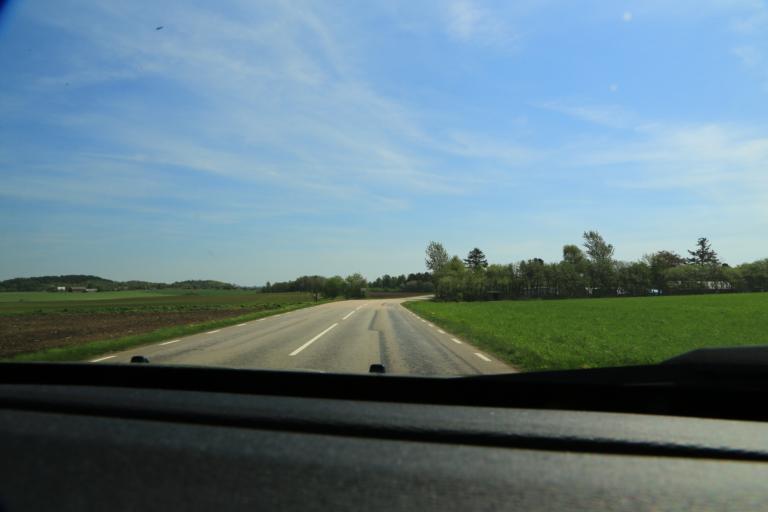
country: SE
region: Halland
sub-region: Varbergs Kommun
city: Varberg
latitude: 57.1351
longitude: 12.3121
